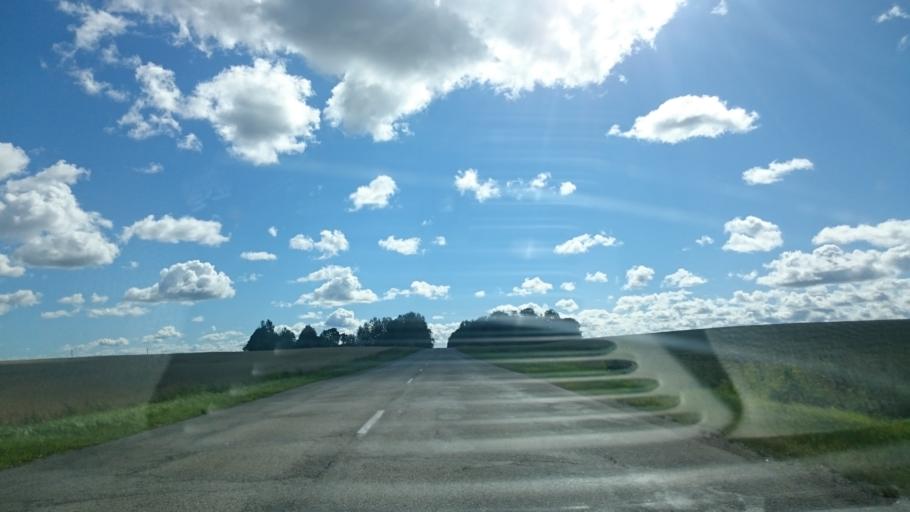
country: LV
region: Aizpute
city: Aizpute
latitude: 56.8342
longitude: 21.7547
